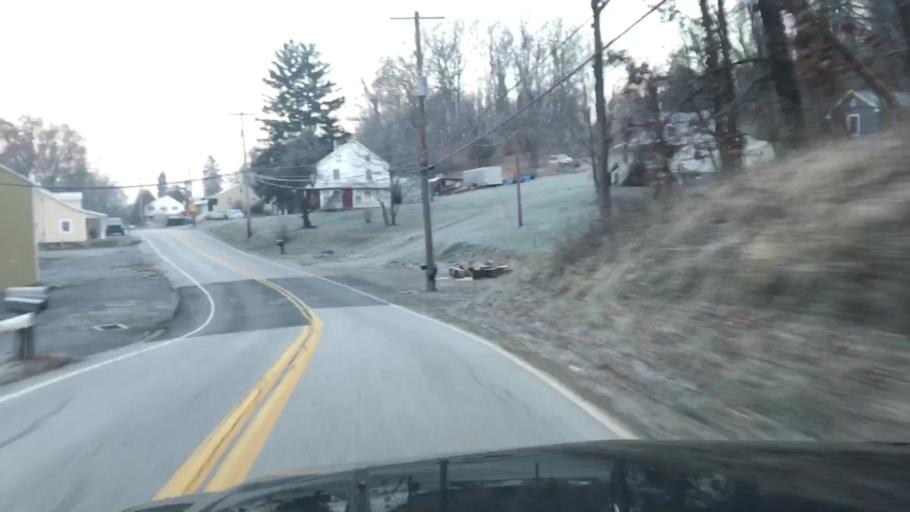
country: US
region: Pennsylvania
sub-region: Cumberland County
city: Lower Allen
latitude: 40.1861
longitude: -76.8866
